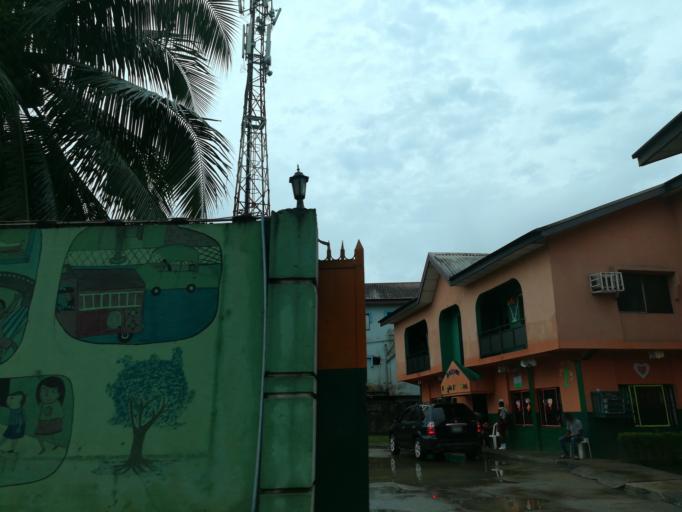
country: NG
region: Rivers
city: Port Harcourt
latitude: 4.8619
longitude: 7.0390
